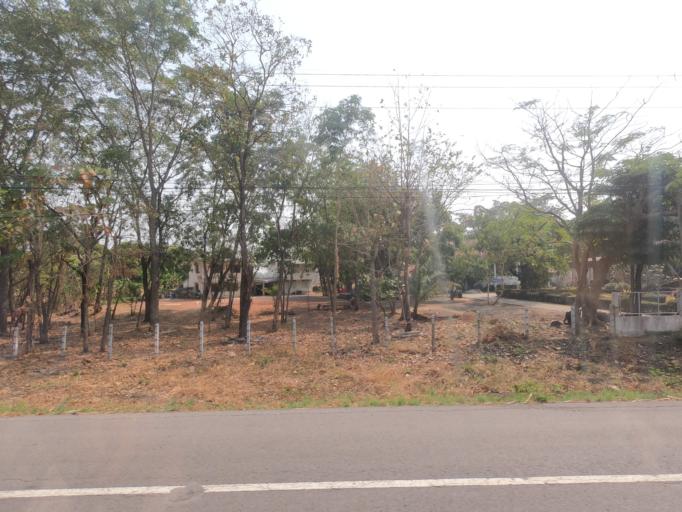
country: TH
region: Nakhon Ratchasima
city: Non Daeng
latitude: 15.3604
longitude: 102.4521
